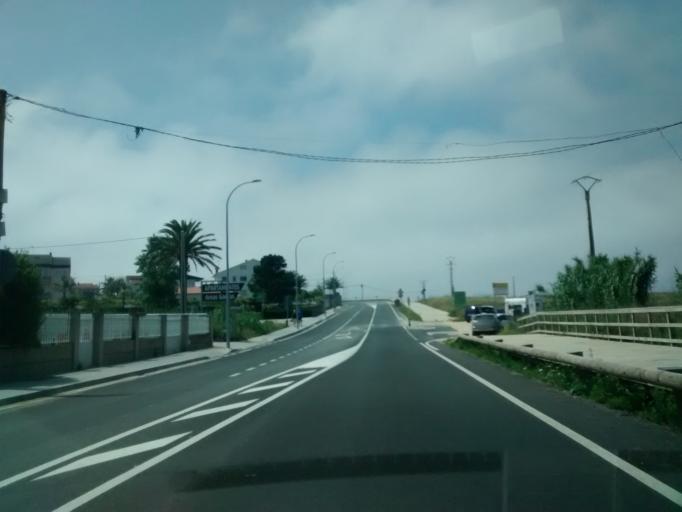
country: ES
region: Galicia
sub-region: Provincia de Pontevedra
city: O Grove
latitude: 42.4307
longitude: -8.8725
